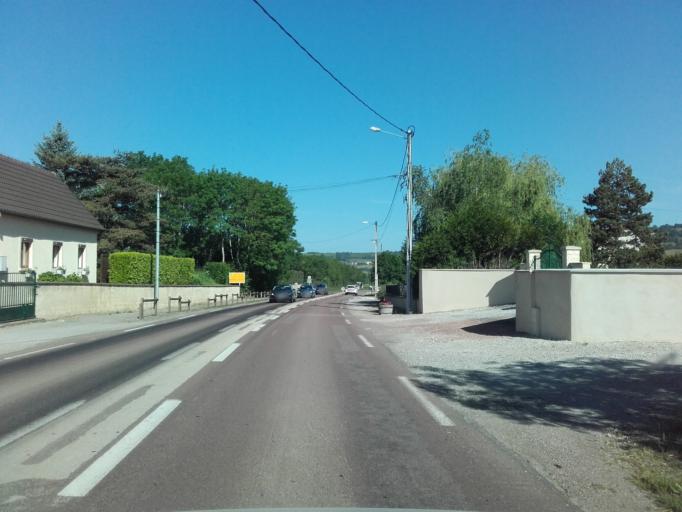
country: FR
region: Bourgogne
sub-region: Departement de la Cote-d'Or
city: Nolay
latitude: 46.9448
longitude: 4.6477
